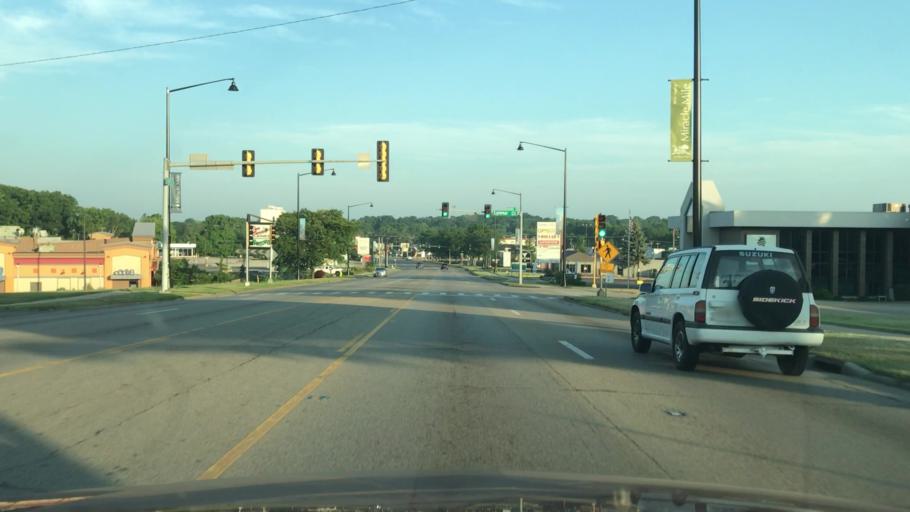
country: US
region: Illinois
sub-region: Winnebago County
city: Loves Park
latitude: 42.2651
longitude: -89.0342
